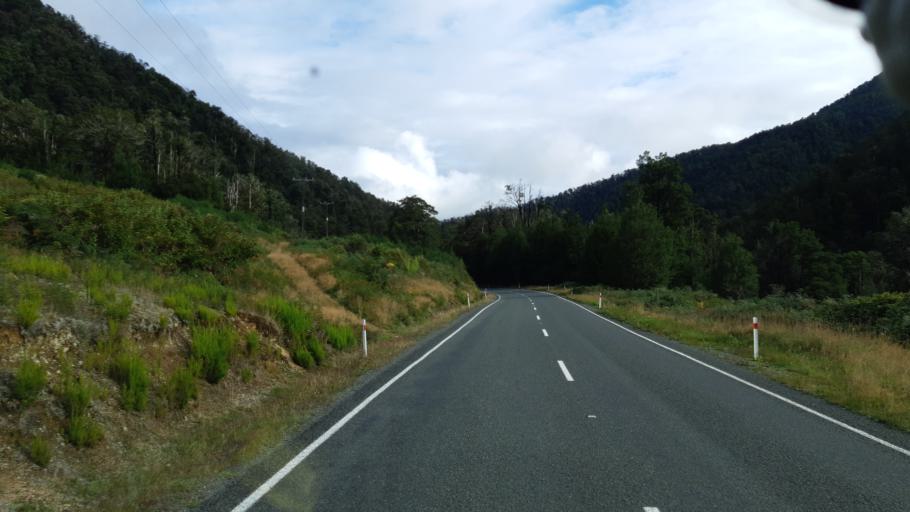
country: NZ
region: West Coast
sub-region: Buller District
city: Westport
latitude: -41.9996
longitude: 172.2261
